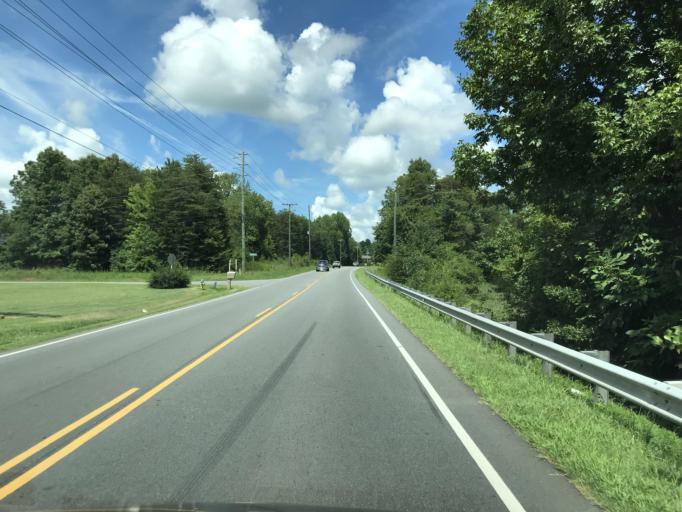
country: US
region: North Carolina
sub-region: Lincoln County
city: Pumpkin Center
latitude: 35.5139
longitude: -81.1543
